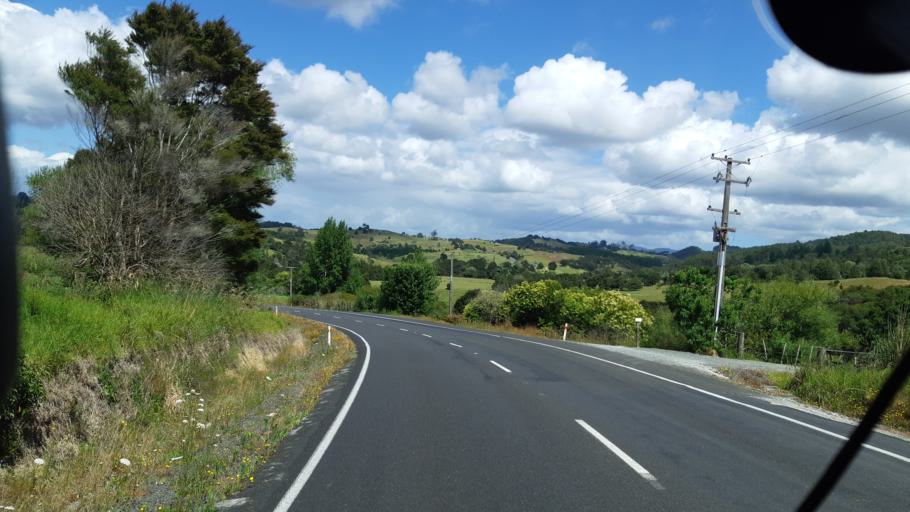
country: NZ
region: Northland
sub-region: Far North District
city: Waimate North
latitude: -35.2978
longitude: 173.6340
